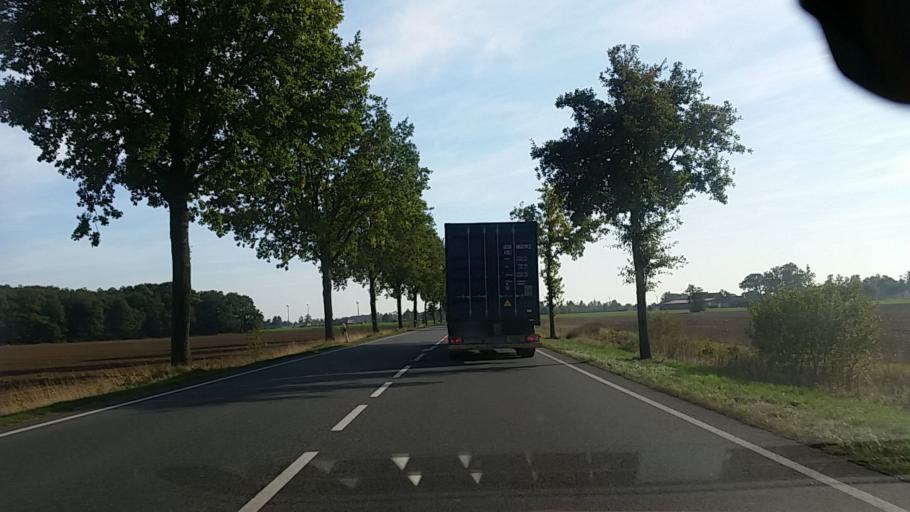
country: DE
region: Lower Saxony
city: Broeckel
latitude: 52.5332
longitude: 10.2157
